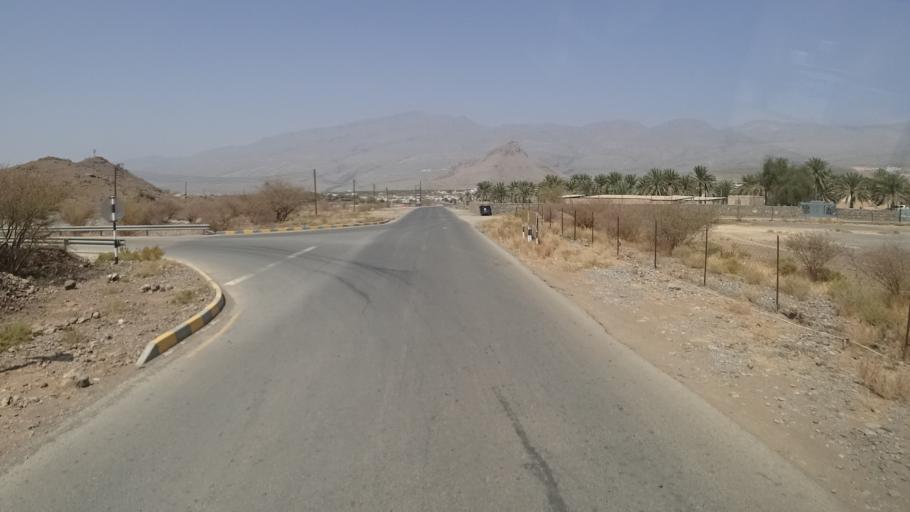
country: OM
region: Muhafazat ad Dakhiliyah
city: Bahla'
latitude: 23.0816
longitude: 57.3132
